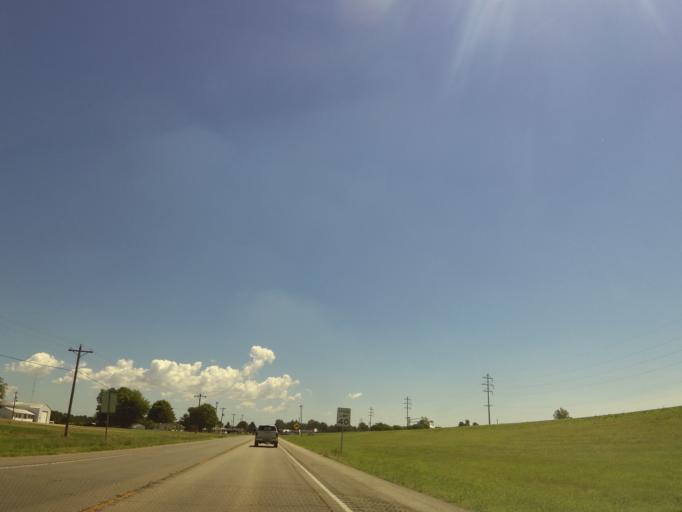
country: US
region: Missouri
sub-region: New Madrid County
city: New Madrid
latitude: 36.5792
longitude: -89.5599
